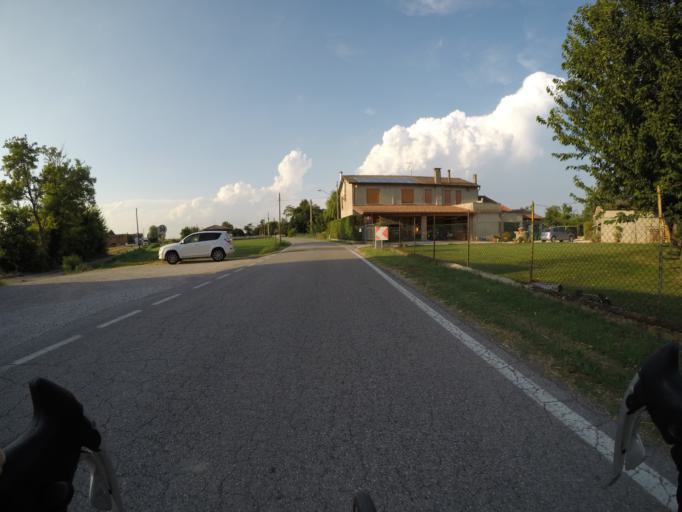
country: IT
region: Veneto
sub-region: Provincia di Rovigo
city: San Bellino
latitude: 45.0478
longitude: 11.5869
